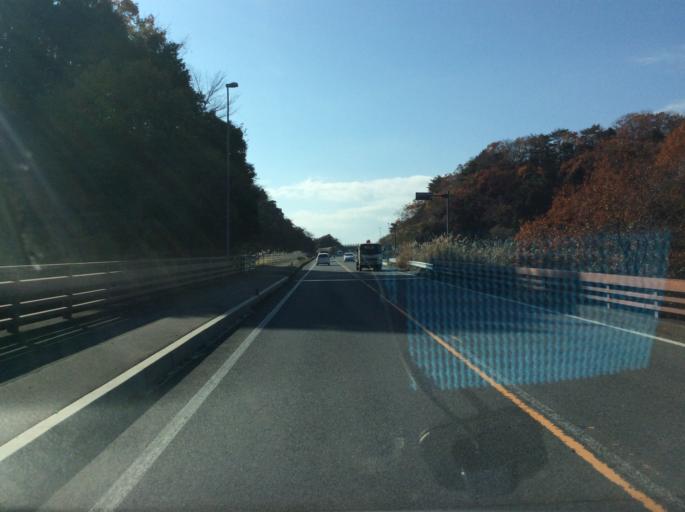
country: JP
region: Fukushima
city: Iwaki
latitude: 37.0410
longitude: 140.9318
